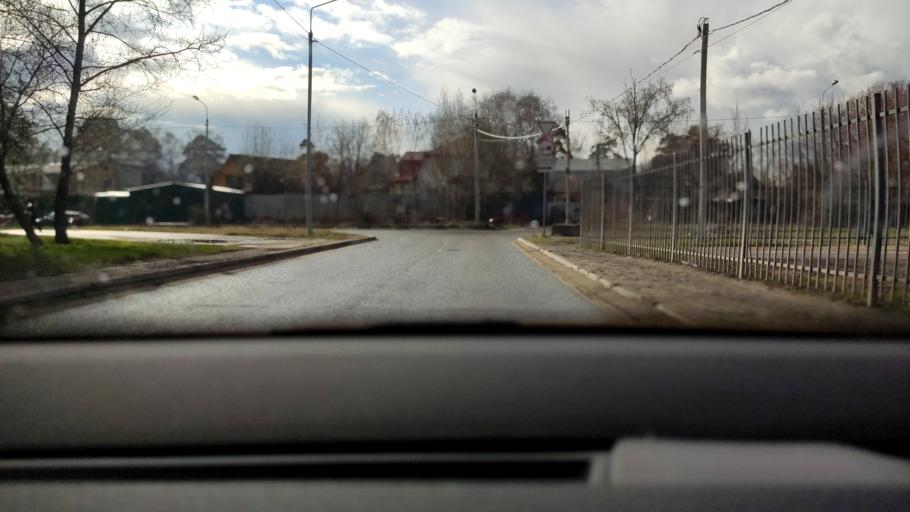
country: RU
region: Moskovskaya
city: Saltykovka
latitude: 55.7453
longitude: 37.9488
